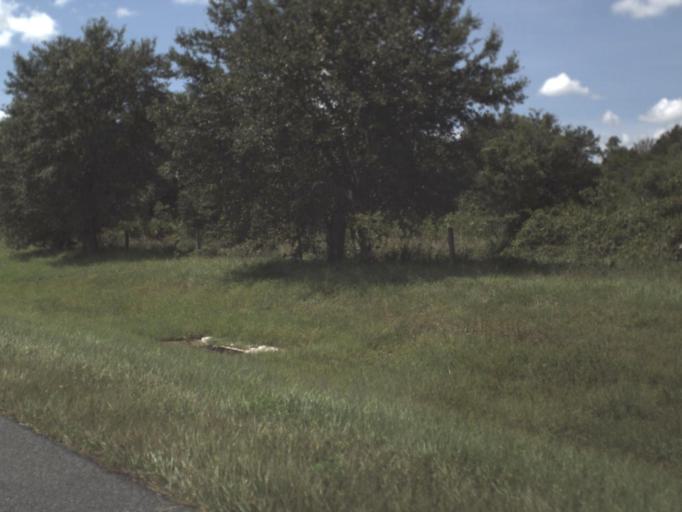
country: US
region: Florida
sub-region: Charlotte County
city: Harbour Heights
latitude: 27.0494
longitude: -81.9586
